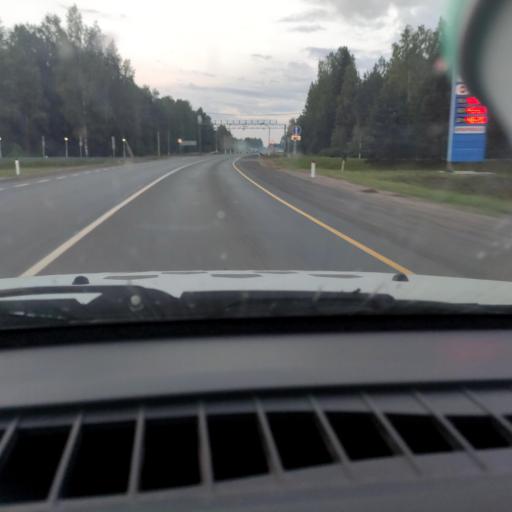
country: RU
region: Kirov
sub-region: Kirovo-Chepetskiy Rayon
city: Kirov
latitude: 58.6845
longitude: 49.6404
